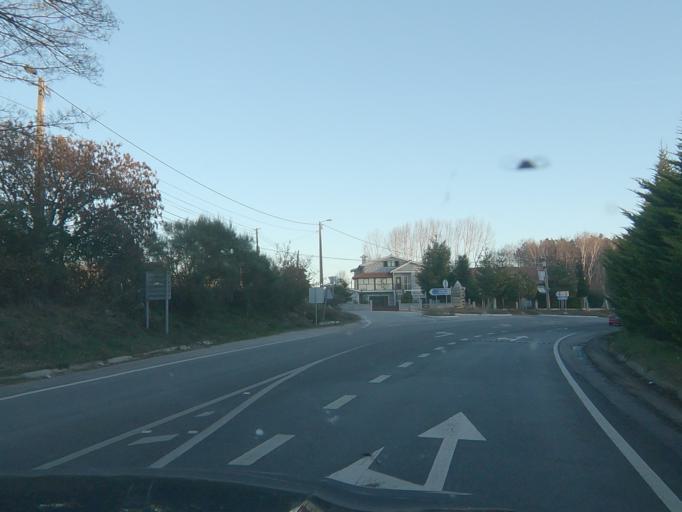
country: PT
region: Vila Real
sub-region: Vila Pouca de Aguiar
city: Vila Pouca de Aguiar
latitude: 41.4935
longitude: -7.6701
